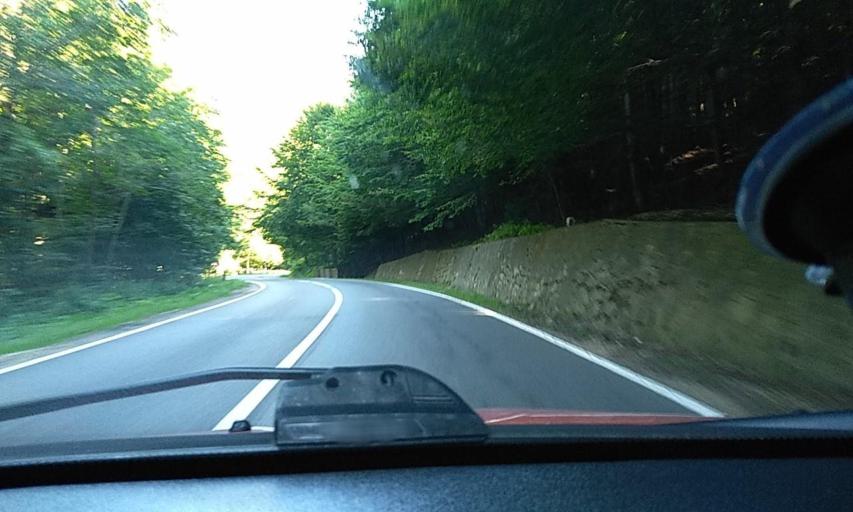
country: RO
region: Brasov
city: Crivina
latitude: 45.4718
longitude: 25.9343
